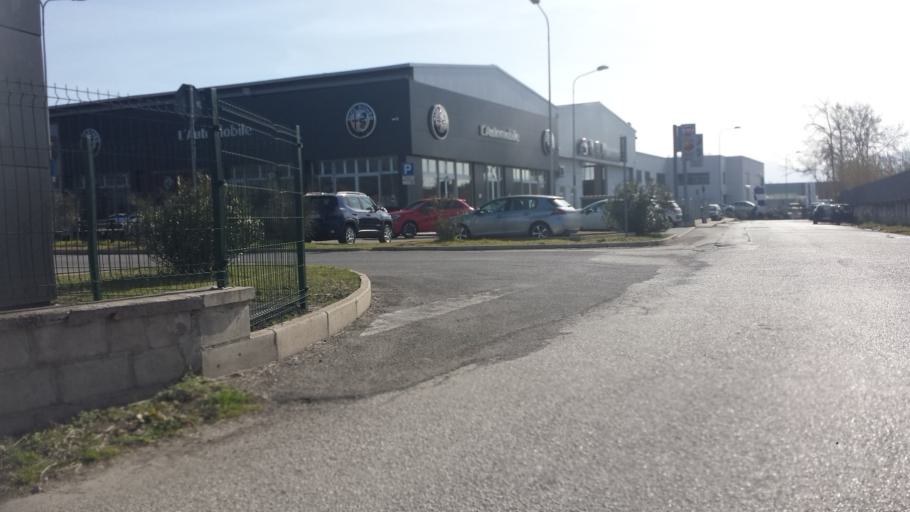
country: IT
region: Umbria
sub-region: Provincia di Terni
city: Terni
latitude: 42.5672
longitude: 12.5995
